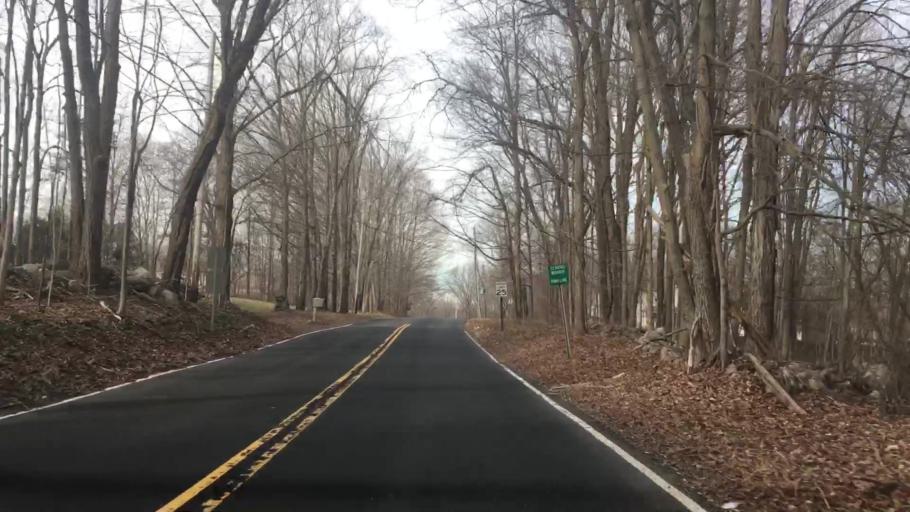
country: US
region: Connecticut
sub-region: Fairfield County
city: Newtown
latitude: 41.3648
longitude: -73.2413
